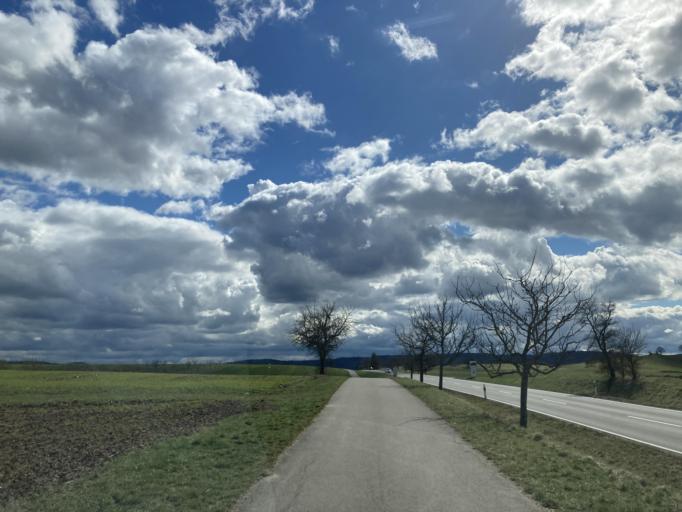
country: DE
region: Baden-Wuerttemberg
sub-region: Tuebingen Region
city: Hirrlingen
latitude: 48.3982
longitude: 8.8832
